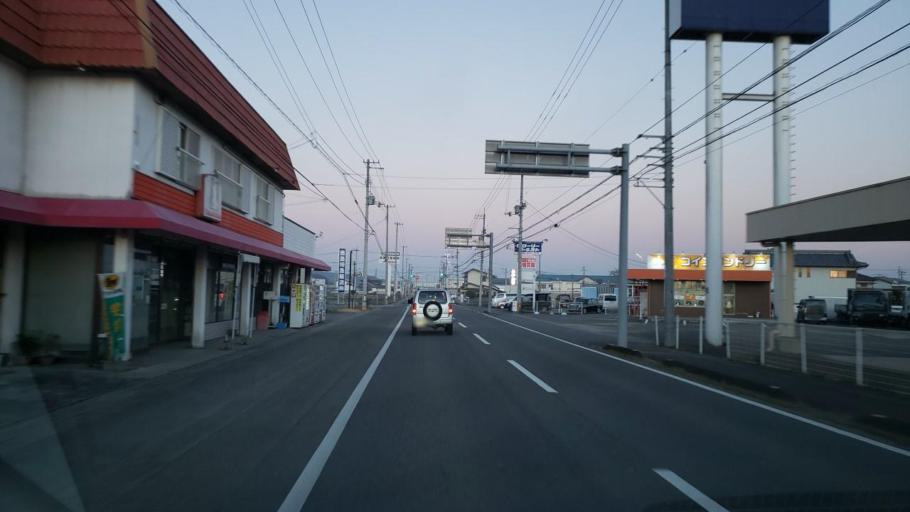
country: JP
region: Tokushima
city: Ishii
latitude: 34.1168
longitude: 134.4253
